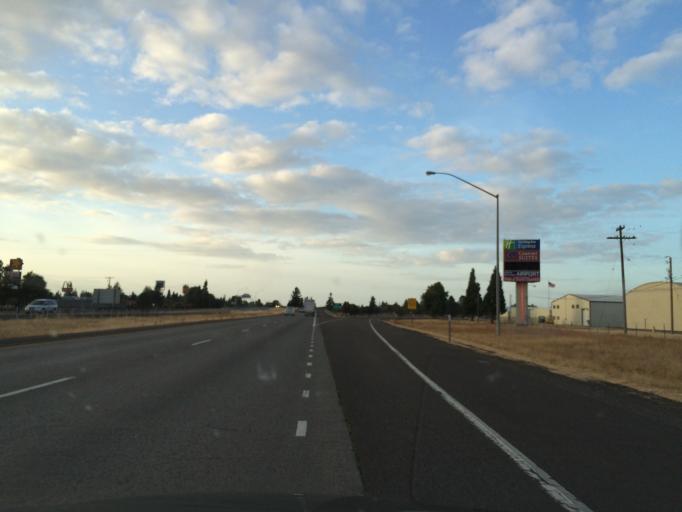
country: US
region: Oregon
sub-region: Linn County
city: Millersburg
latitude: 44.6389
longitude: -123.0622
